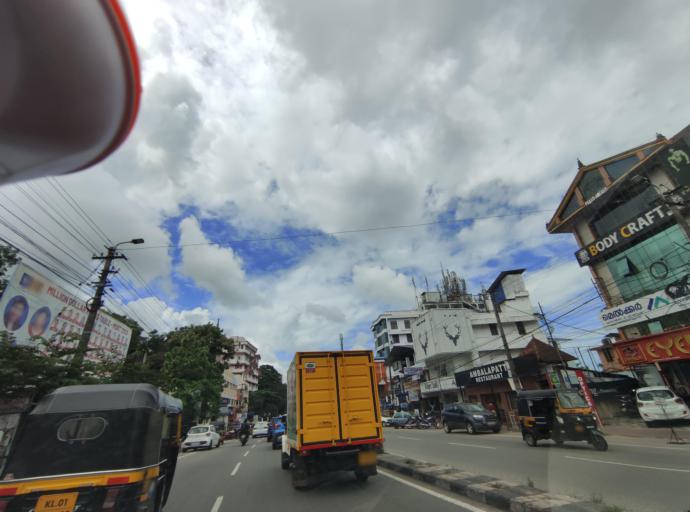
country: IN
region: Kerala
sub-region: Thiruvananthapuram
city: Thiruvananthapuram
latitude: 8.5227
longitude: 76.9408
